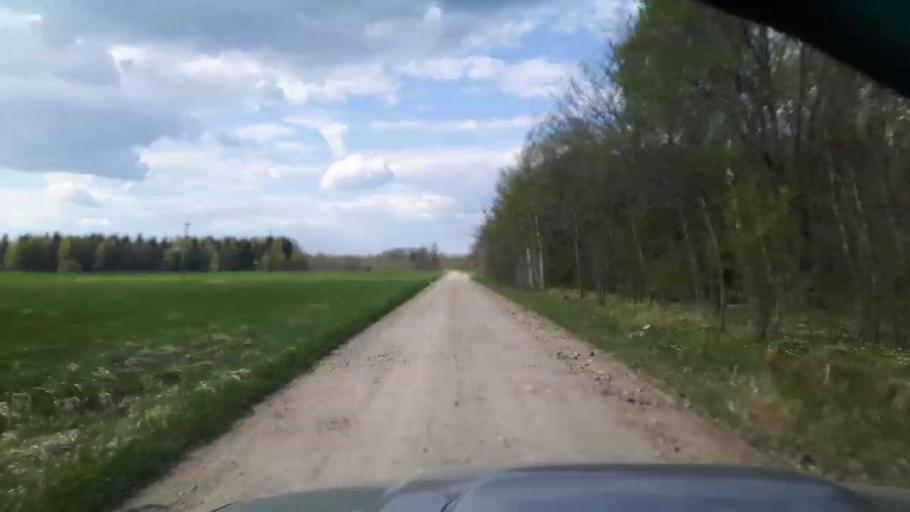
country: EE
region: Paernumaa
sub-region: Sindi linn
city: Sindi
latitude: 58.4418
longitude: 24.7577
